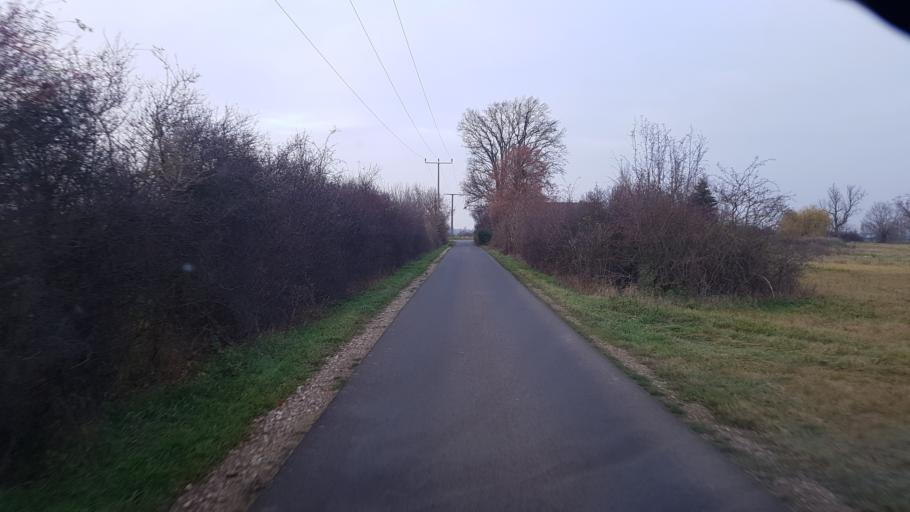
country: DE
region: Brandenburg
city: Ziltendorf
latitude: 52.2217
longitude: 14.6316
